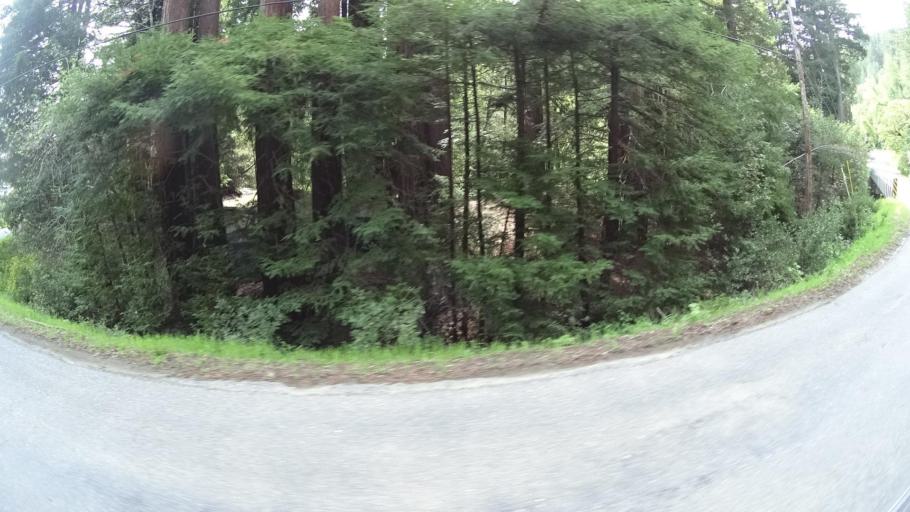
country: US
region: California
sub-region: Humboldt County
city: Redway
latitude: 40.0690
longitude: -123.8300
